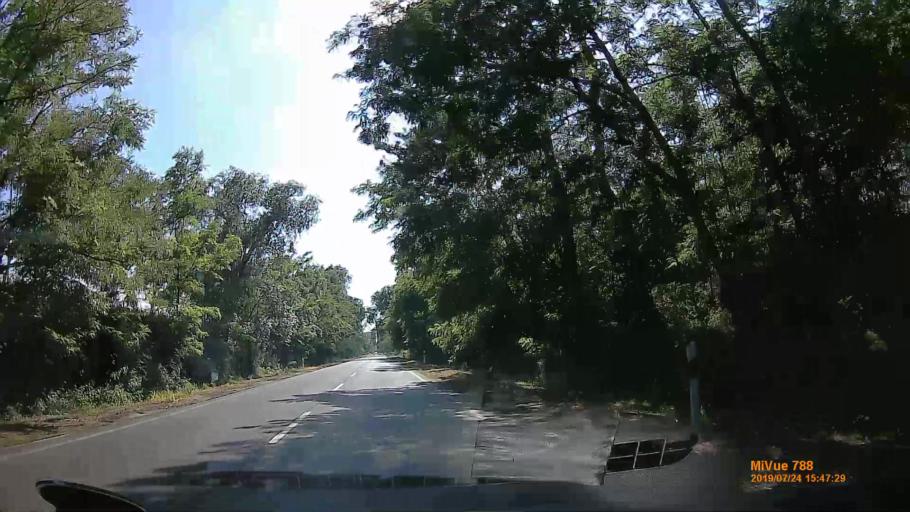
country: HU
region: Szabolcs-Szatmar-Bereg
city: Nyirmada
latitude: 48.0772
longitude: 22.2496
